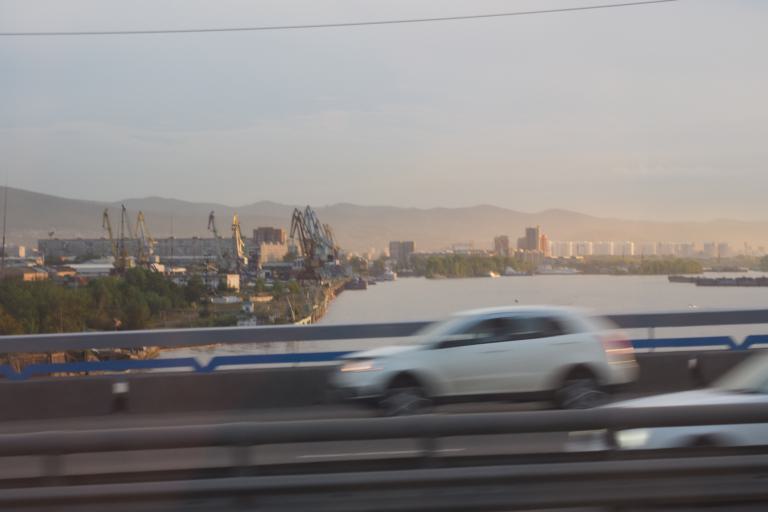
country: RU
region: Krasnoyarskiy
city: Krasnoyarsk
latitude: 56.0178
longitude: 92.9533
